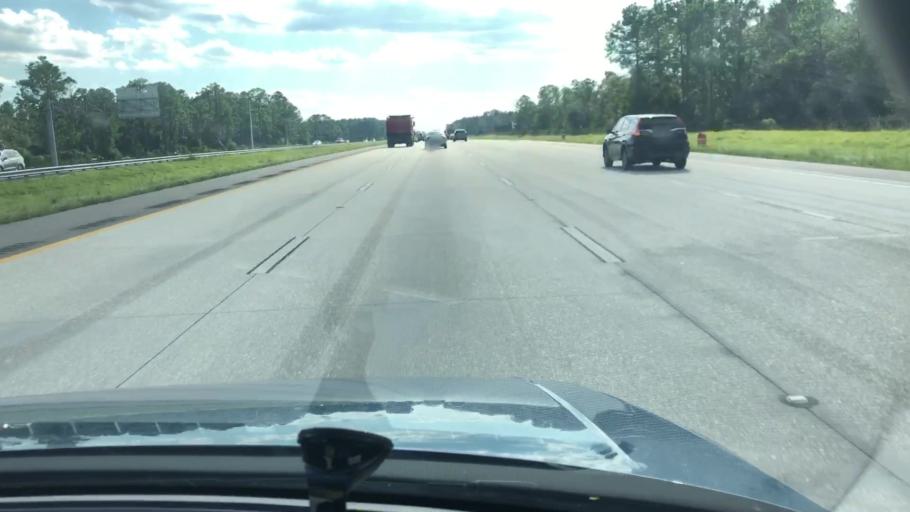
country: US
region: Florida
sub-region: Volusia County
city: Samsula-Spruce Creek
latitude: 29.1309
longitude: -81.1247
